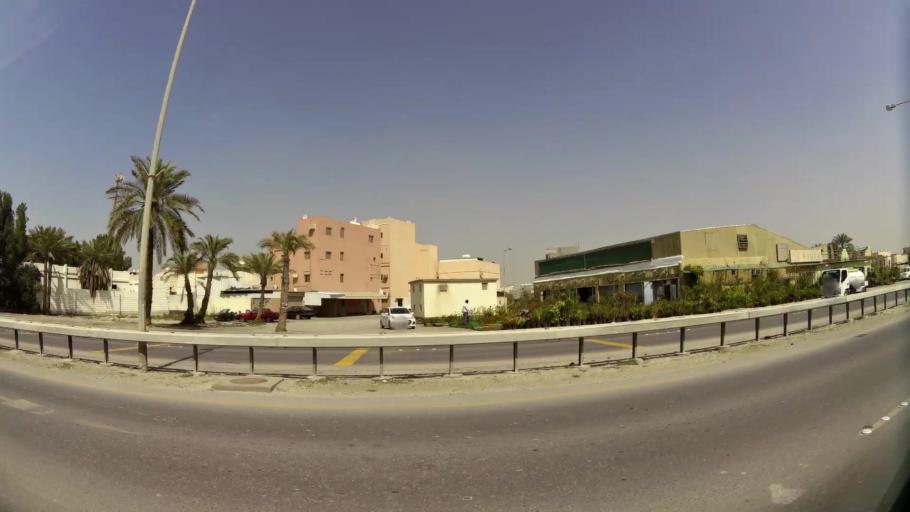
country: BH
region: Northern
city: Madinat `Isa
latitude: 26.1949
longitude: 50.4625
